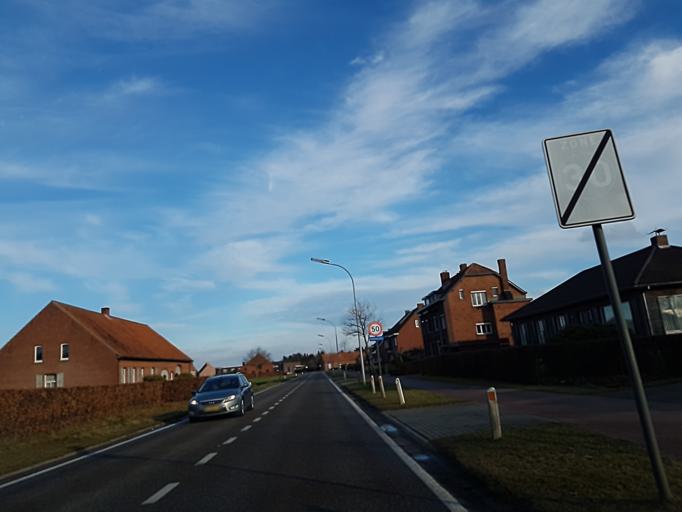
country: BE
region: Flanders
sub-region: Provincie Antwerpen
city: Retie
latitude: 51.2685
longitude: 5.0917
